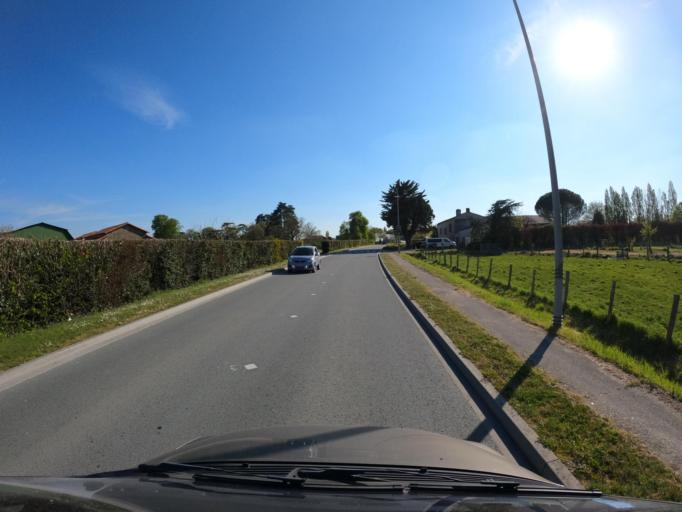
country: FR
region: Pays de la Loire
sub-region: Departement de la Vendee
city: Mortagne-sur-Sevre
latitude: 46.9987
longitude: -0.9422
